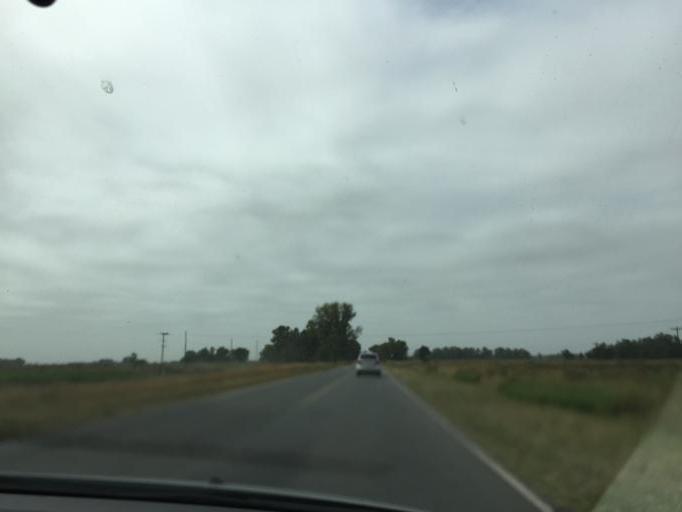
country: AR
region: Buenos Aires
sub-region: Partido de Las Flores
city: Las Flores
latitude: -36.1913
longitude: -59.0559
